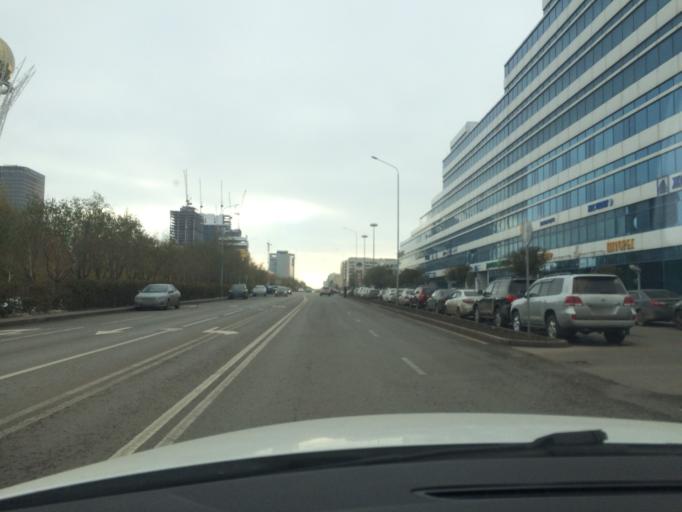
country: KZ
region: Astana Qalasy
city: Astana
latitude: 51.1307
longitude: 71.4294
